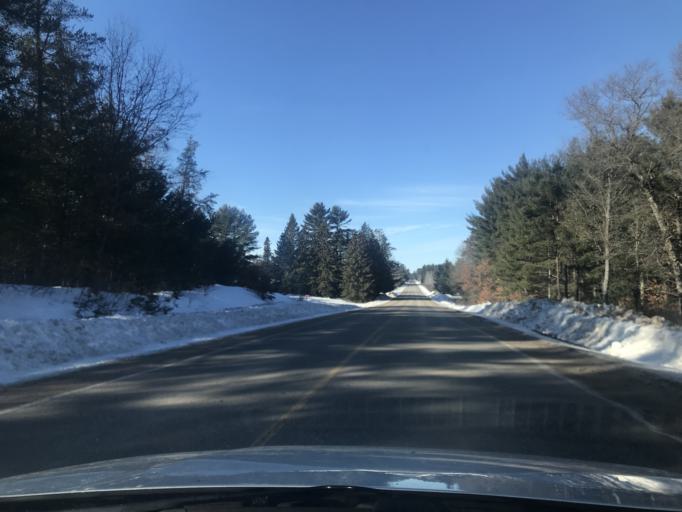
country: US
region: Wisconsin
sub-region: Marinette County
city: Niagara
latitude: 45.4266
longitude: -88.0779
